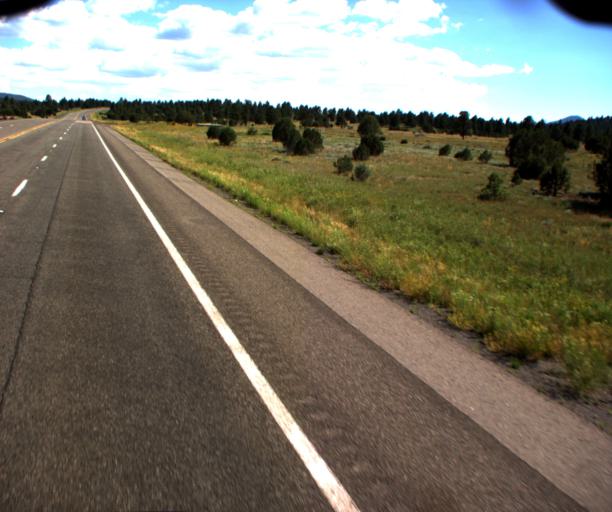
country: US
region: Arizona
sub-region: Coconino County
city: Williams
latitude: 35.3060
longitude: -112.1447
